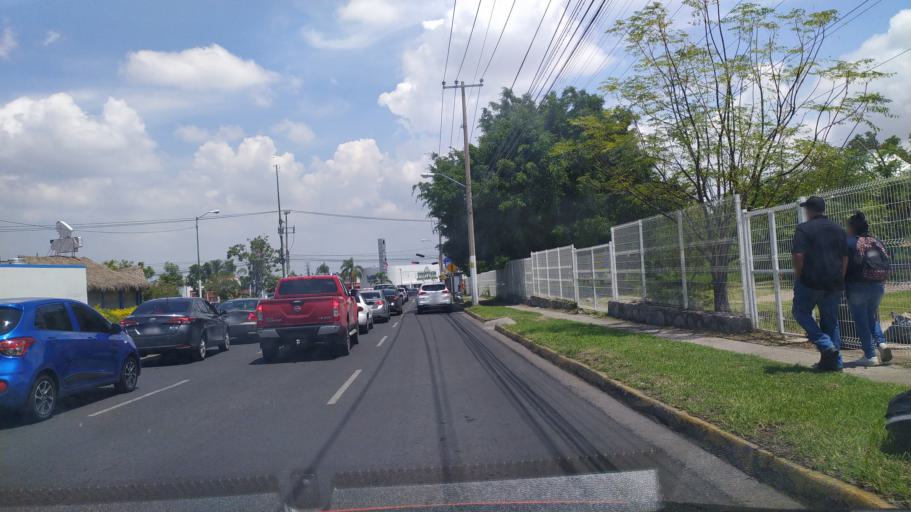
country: MX
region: Jalisco
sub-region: Zapopan
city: Zapopan
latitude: 20.7539
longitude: -103.3850
